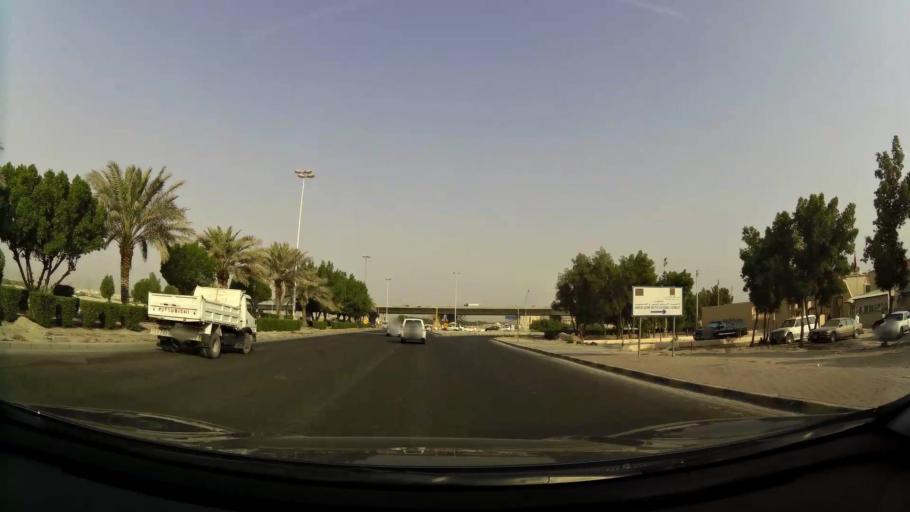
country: KW
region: Al Asimah
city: Ar Rabiyah
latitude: 29.3184
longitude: 47.8046
